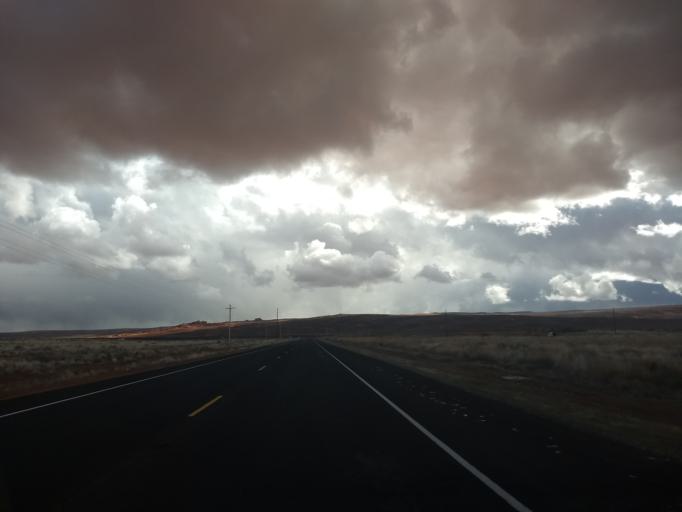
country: US
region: Utah
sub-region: Washington County
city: Hurricane
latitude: 37.1263
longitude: -113.3927
